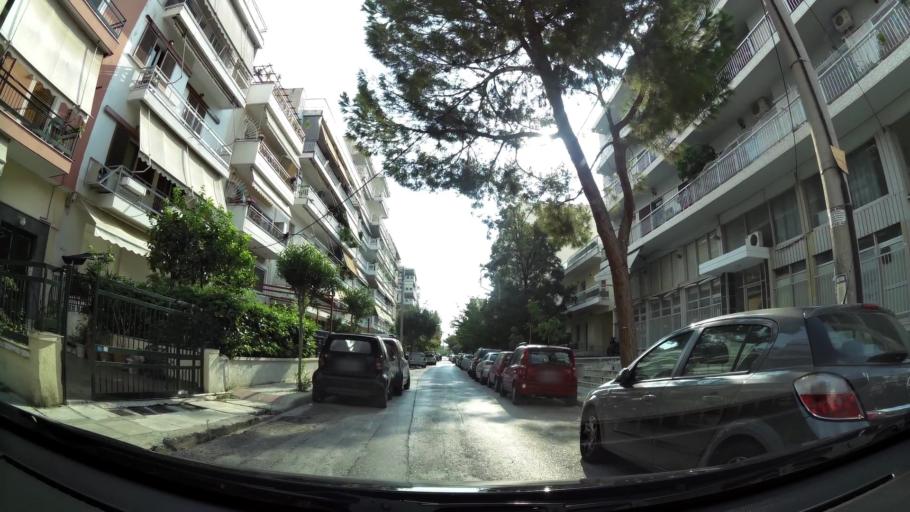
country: GR
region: Attica
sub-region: Nomarchia Athinas
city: Moskhaton
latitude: 37.9439
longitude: 23.6870
